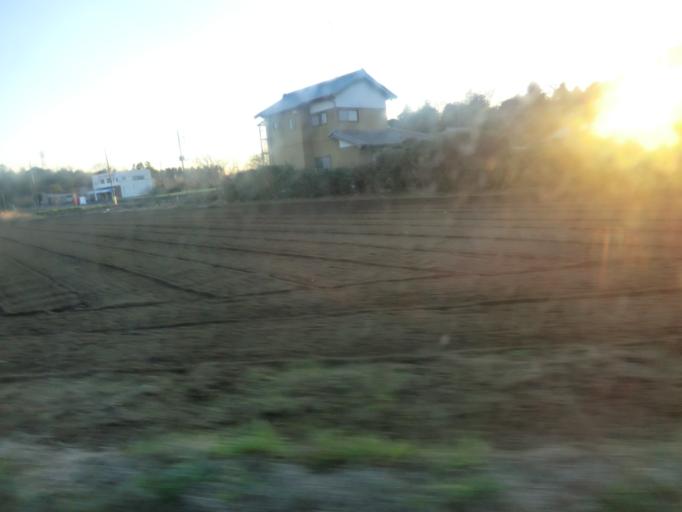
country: JP
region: Ibaraki
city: Ushiku
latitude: 35.9975
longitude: 140.1258
